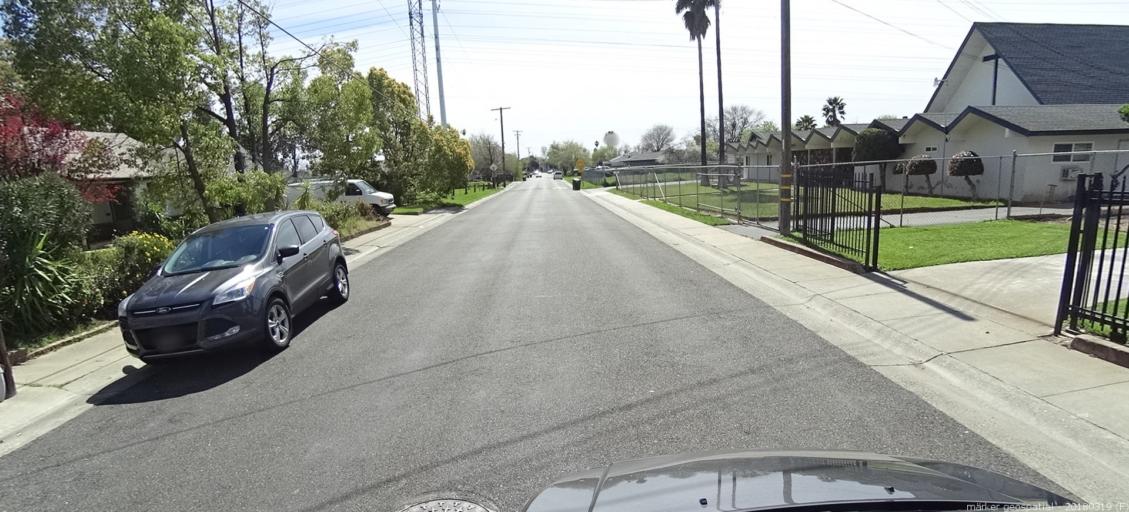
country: US
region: California
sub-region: Sacramento County
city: Parkway
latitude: 38.5092
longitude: -121.4539
